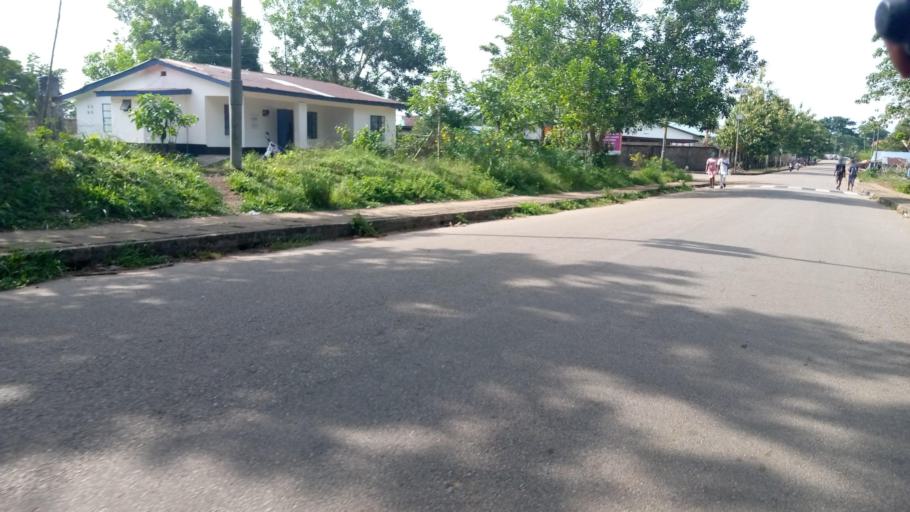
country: SL
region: Southern Province
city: Pujehun
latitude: 7.3517
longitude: -11.7198
